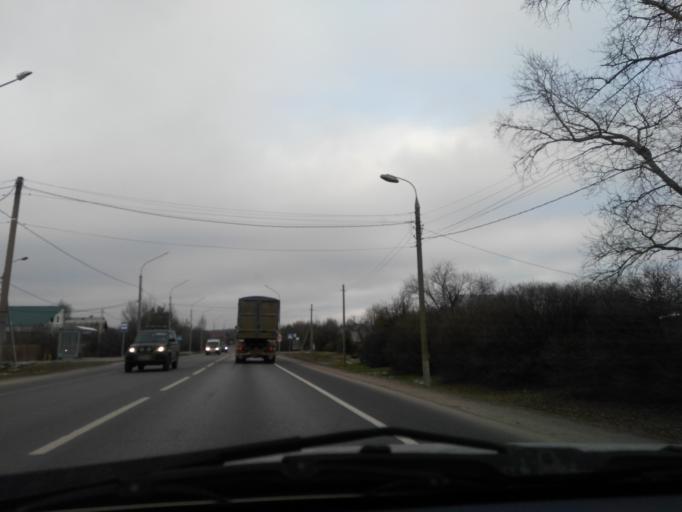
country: RU
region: Moskovskaya
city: Troitsk
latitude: 55.3689
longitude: 37.2009
